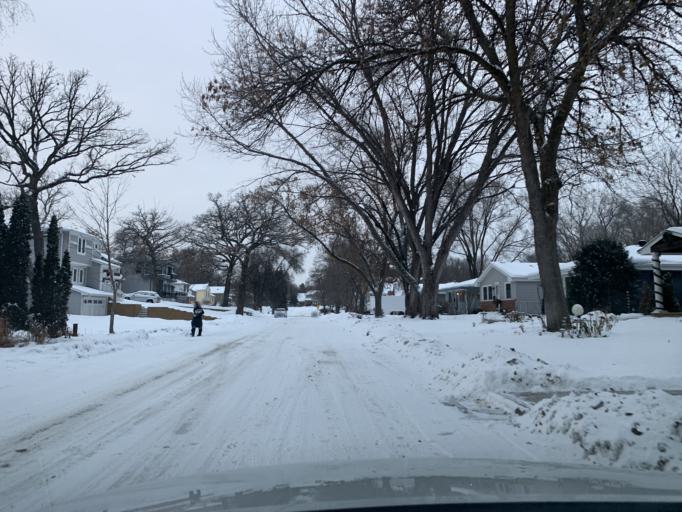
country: US
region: Minnesota
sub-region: Hennepin County
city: Saint Louis Park
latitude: 44.9254
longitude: -93.3404
